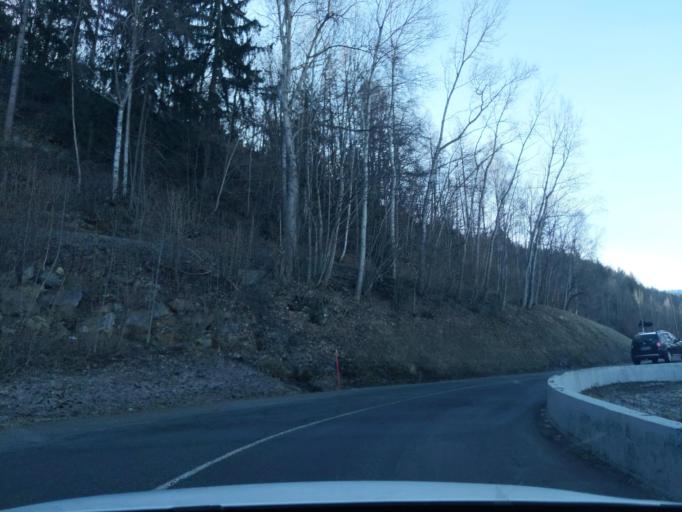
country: FR
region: Rhone-Alpes
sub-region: Departement de la Savoie
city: Bourg-Saint-Maurice
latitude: 45.6034
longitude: 6.7728
